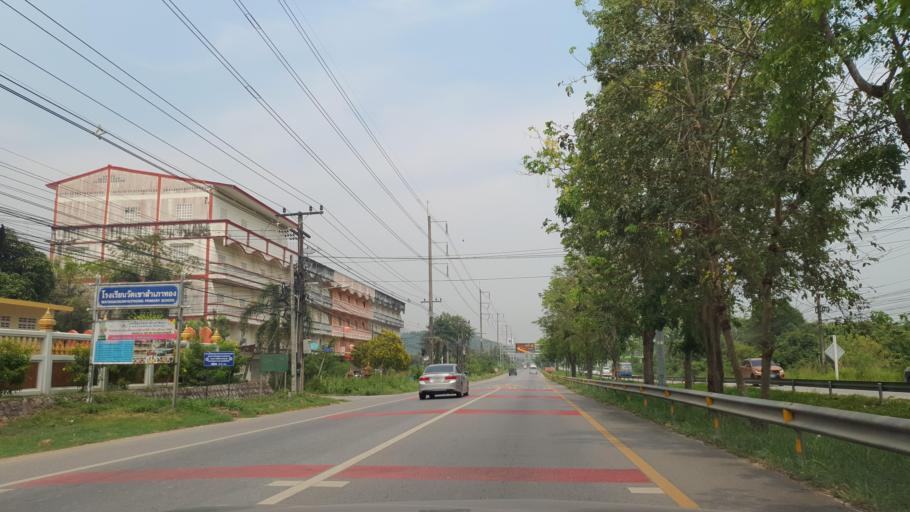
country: TH
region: Rayong
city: Rayong
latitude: 12.6416
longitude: 101.4115
